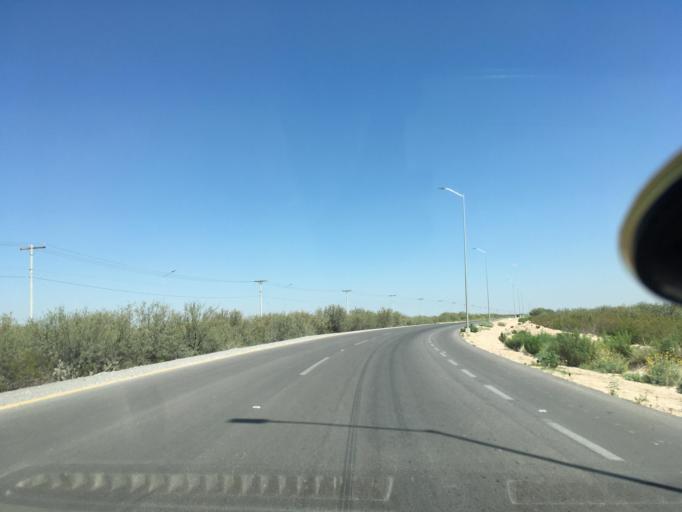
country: MX
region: Coahuila
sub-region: Torreon
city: Fraccionamiento la Noria
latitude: 25.4930
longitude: -103.3237
